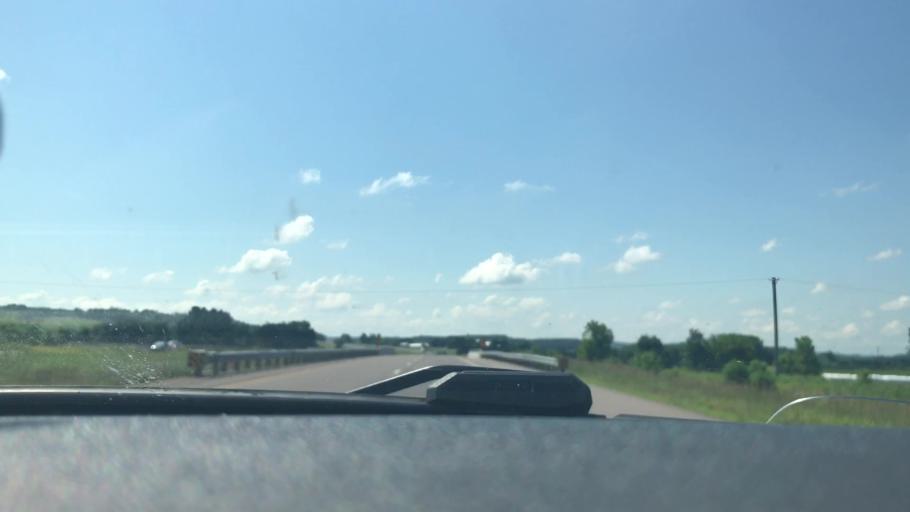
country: US
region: Wisconsin
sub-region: Chippewa County
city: Bloomer
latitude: 45.0576
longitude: -91.4657
